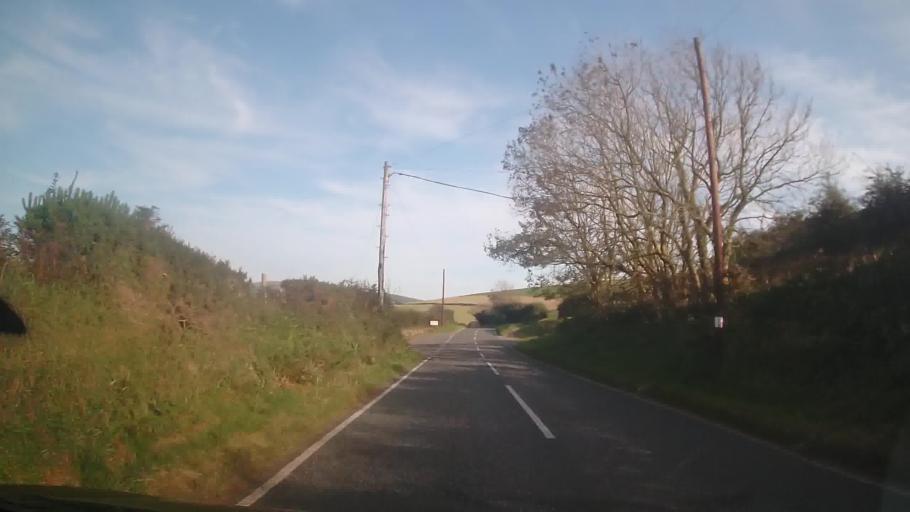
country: GB
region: Wales
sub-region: Pembrokeshire
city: Ambleston
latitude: 51.9658
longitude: -4.8992
